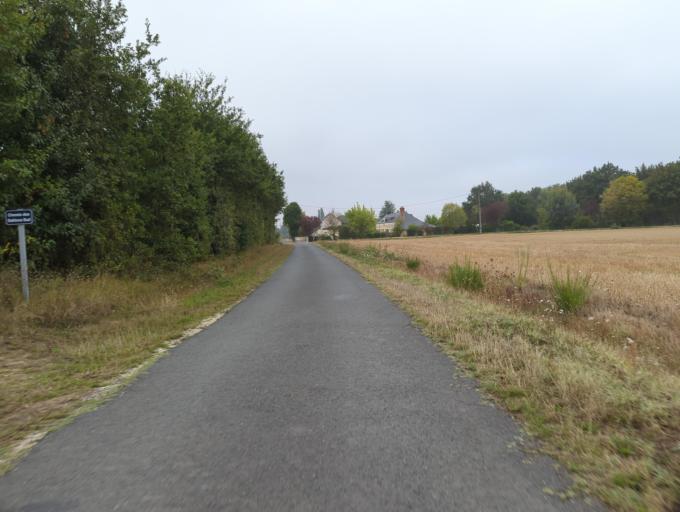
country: FR
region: Pays de la Loire
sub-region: Departement de Maine-et-Loire
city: Le Plessis-Grammoire
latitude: 47.4784
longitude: -0.4410
